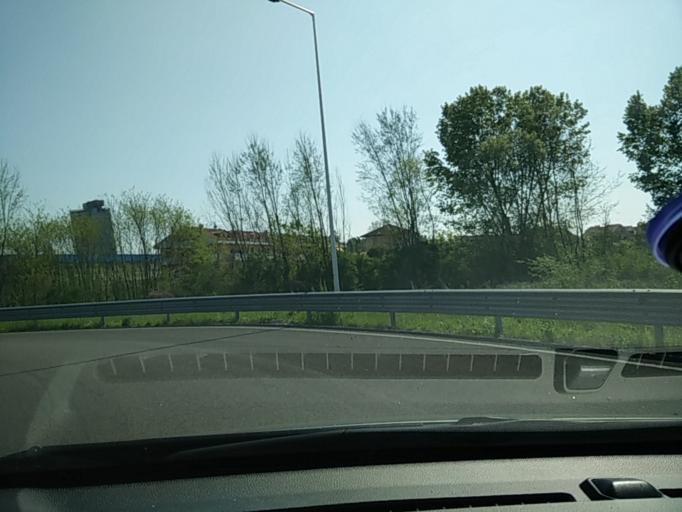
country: IT
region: Veneto
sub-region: Provincia di Padova
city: Cadoneghe
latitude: 45.4211
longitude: 11.9188
